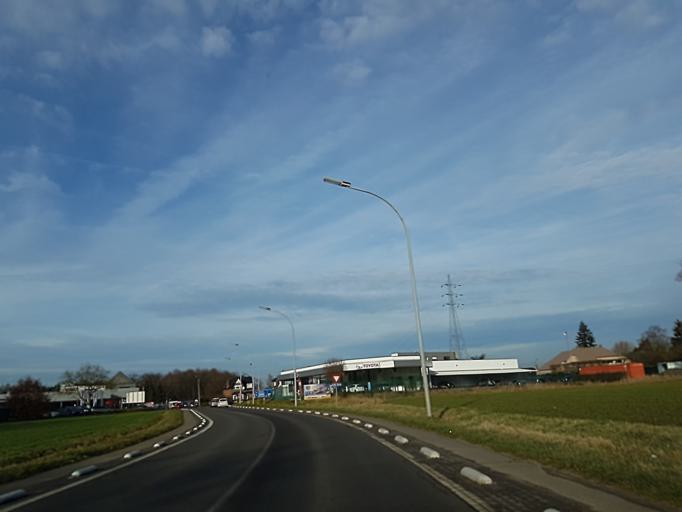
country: BE
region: Flanders
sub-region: Provincie Vlaams-Brabant
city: Haacht
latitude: 50.9788
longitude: 4.6416
